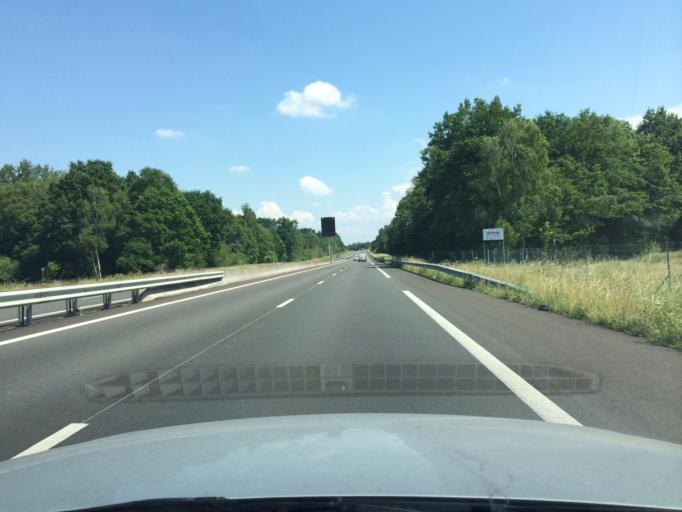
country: FR
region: Lorraine
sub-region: Departement de Meurthe-et-Moselle
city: Chanteheux
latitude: 48.5804
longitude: 6.5977
